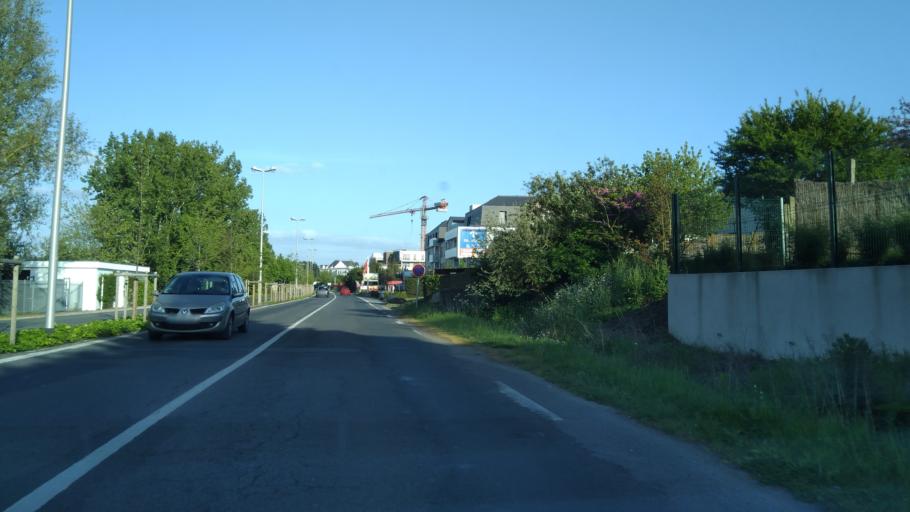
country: FR
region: Pays de la Loire
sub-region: Departement de la Loire-Atlantique
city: Pornichet
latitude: 47.2593
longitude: -2.3298
